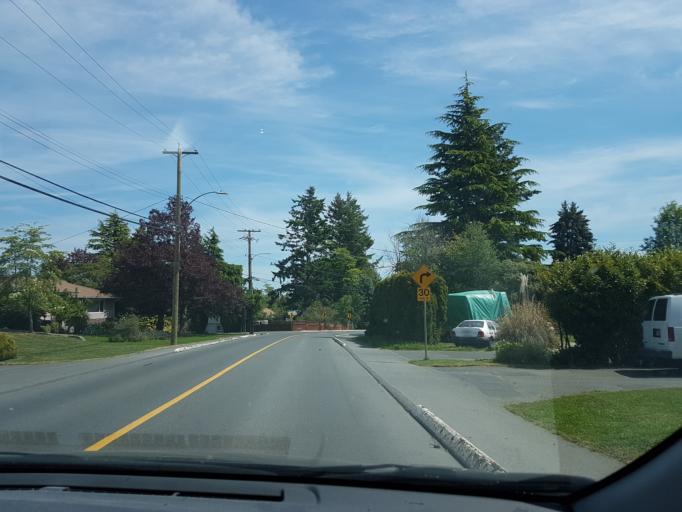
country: CA
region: British Columbia
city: Oak Bay
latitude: 48.4884
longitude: -123.3140
